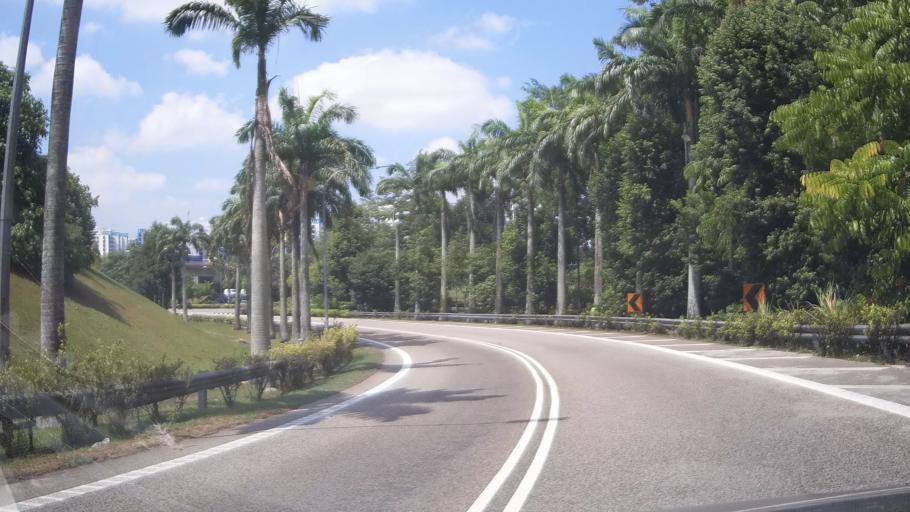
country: MY
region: Johor
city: Johor Bahru
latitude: 1.3922
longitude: 103.7751
